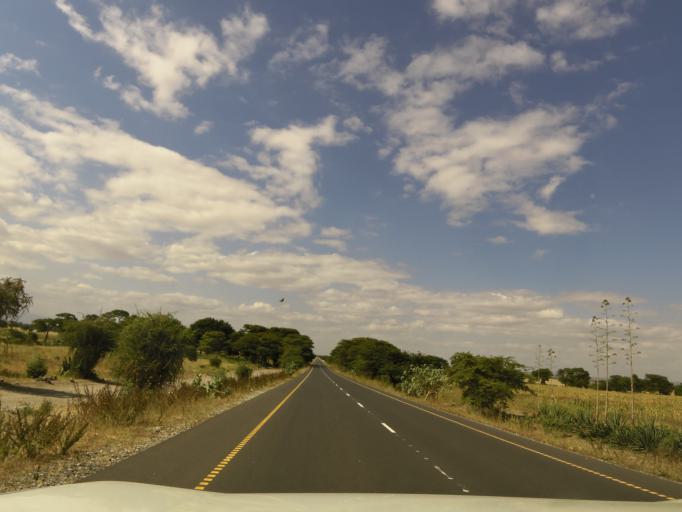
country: TZ
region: Arusha
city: Mto wa Mbu
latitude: -3.6712
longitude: 35.9487
